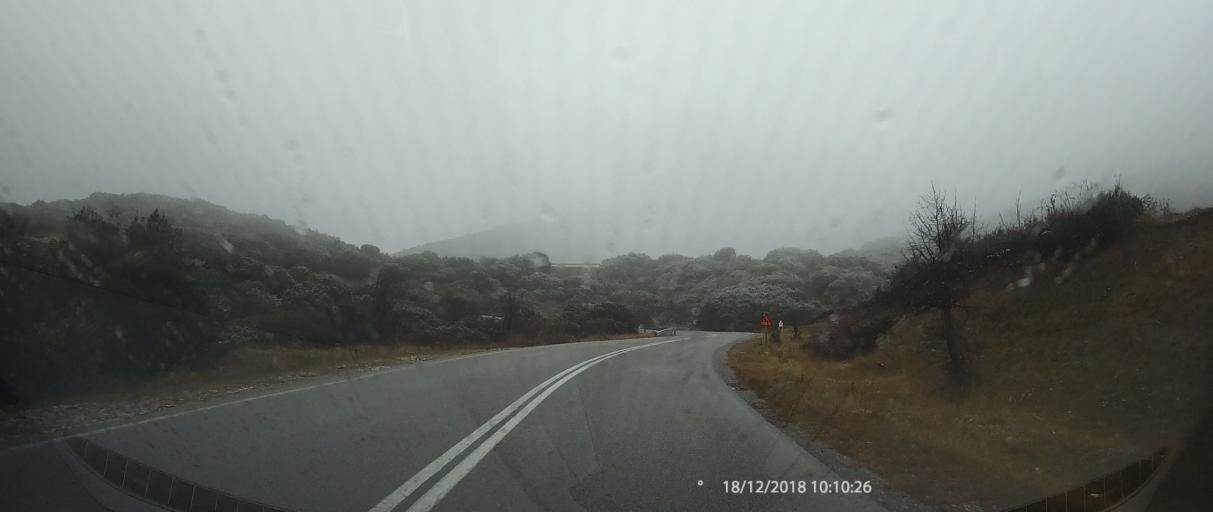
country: GR
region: Thessaly
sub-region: Nomos Larisis
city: Livadi
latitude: 40.0893
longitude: 22.2118
